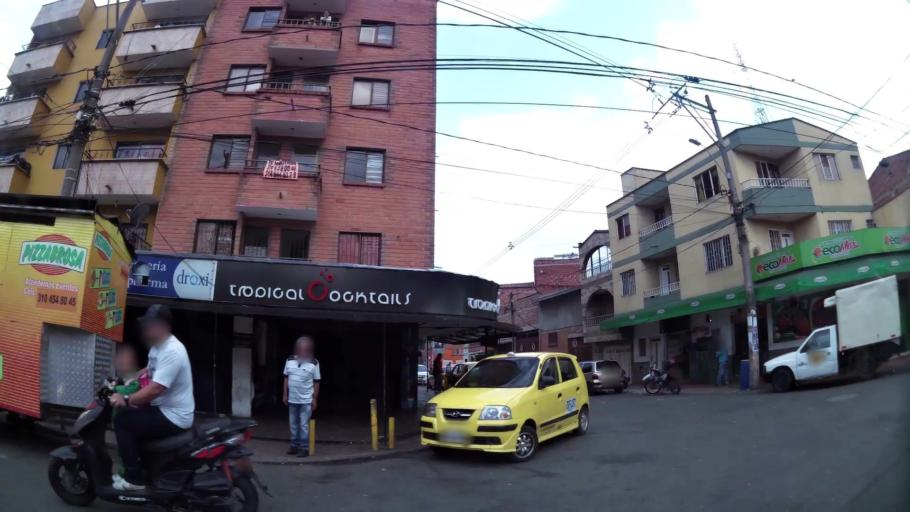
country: CO
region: Antioquia
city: Medellin
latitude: 6.2265
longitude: -75.5851
